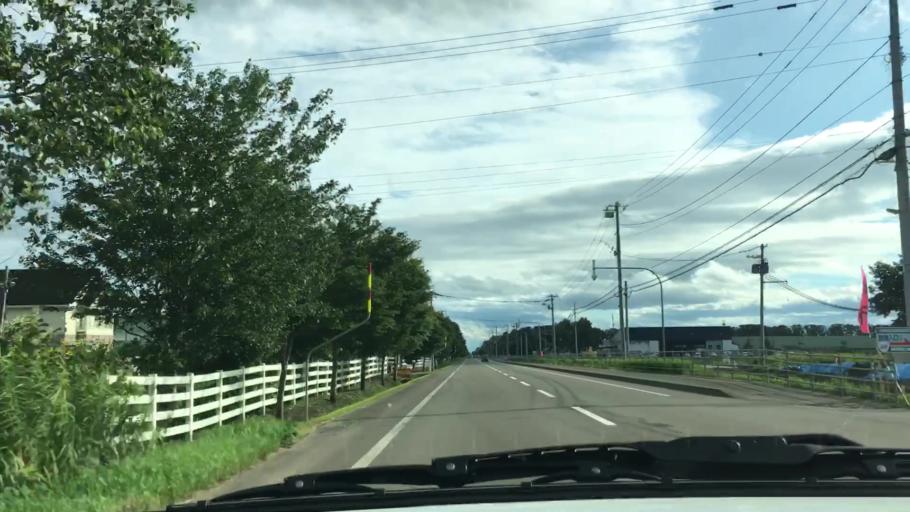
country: JP
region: Hokkaido
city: Otofuke
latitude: 43.2530
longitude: 143.2997
